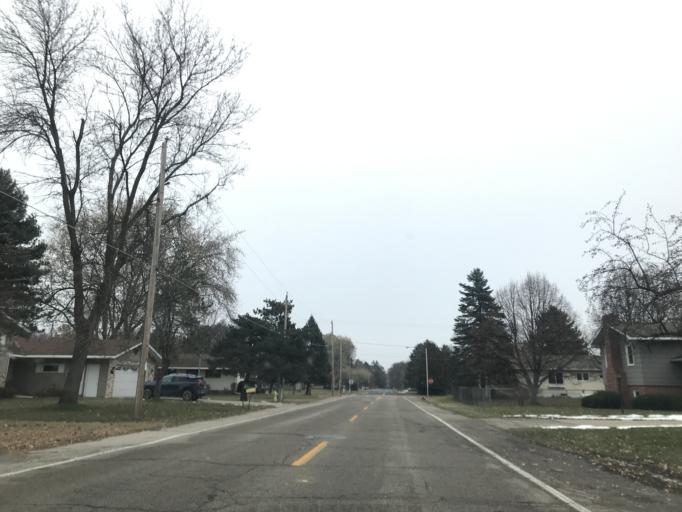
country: US
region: Wisconsin
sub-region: Marinette County
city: Marinette
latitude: 45.0781
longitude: -87.6206
